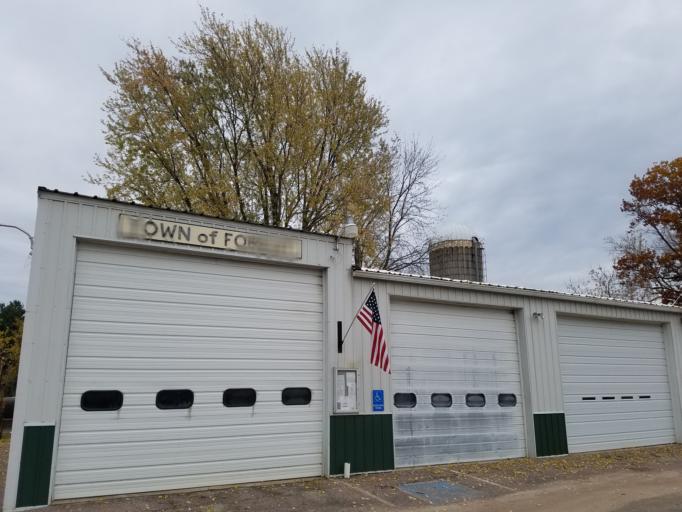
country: US
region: Wisconsin
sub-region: Vernon County
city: Hillsboro
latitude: 43.6715
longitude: -90.4691
